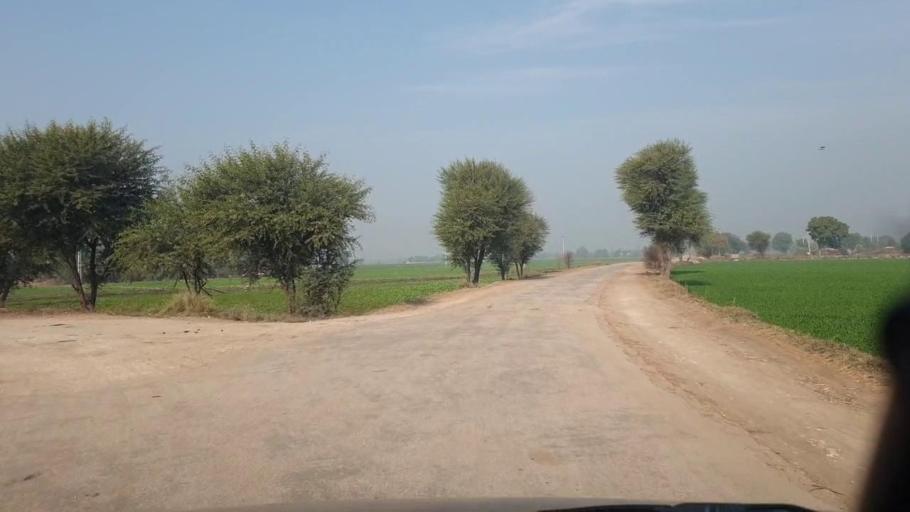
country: PK
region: Sindh
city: Shahdadpur
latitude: 26.0078
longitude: 68.5491
